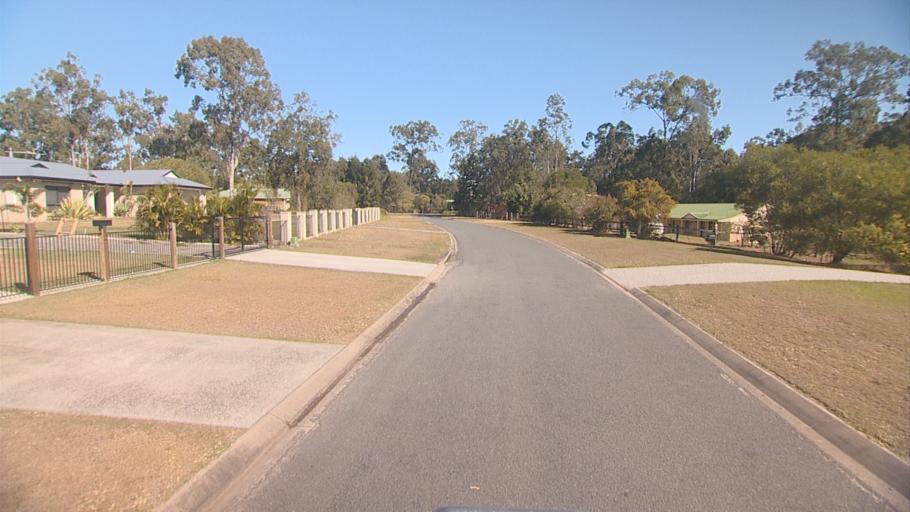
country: AU
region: Queensland
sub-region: Logan
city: North Maclean
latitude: -27.8194
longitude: 152.9542
